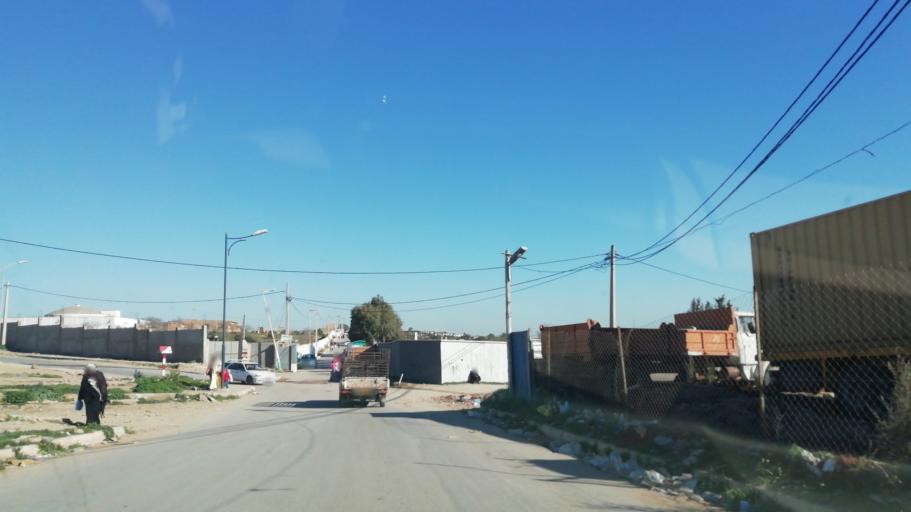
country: DZ
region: Oran
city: Bir el Djir
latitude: 35.7243
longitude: -0.5266
